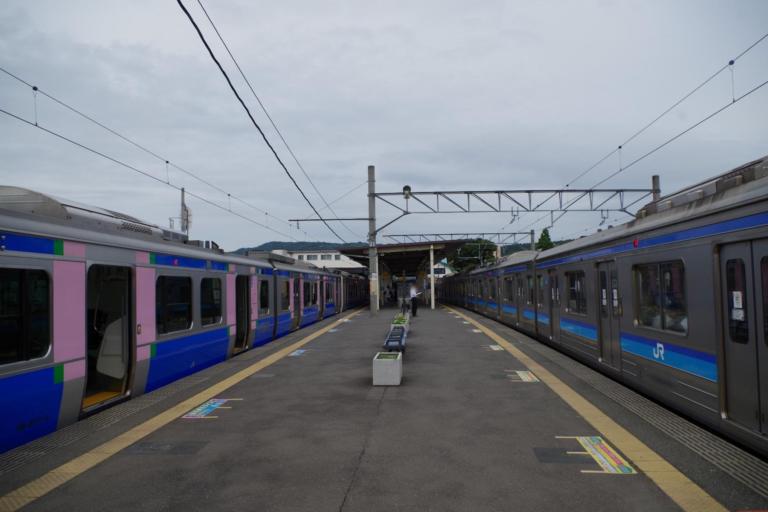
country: JP
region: Miyagi
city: Ishinomaki
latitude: 38.4353
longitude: 141.3026
